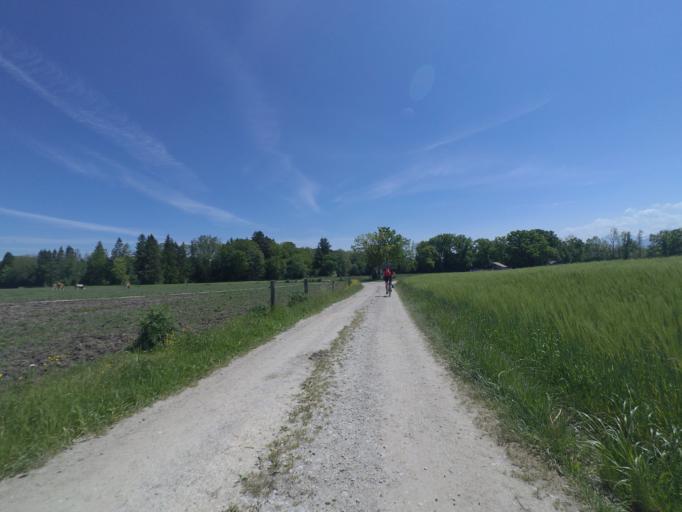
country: DE
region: Bavaria
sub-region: Upper Bavaria
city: Petting
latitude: 47.9501
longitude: 12.7828
